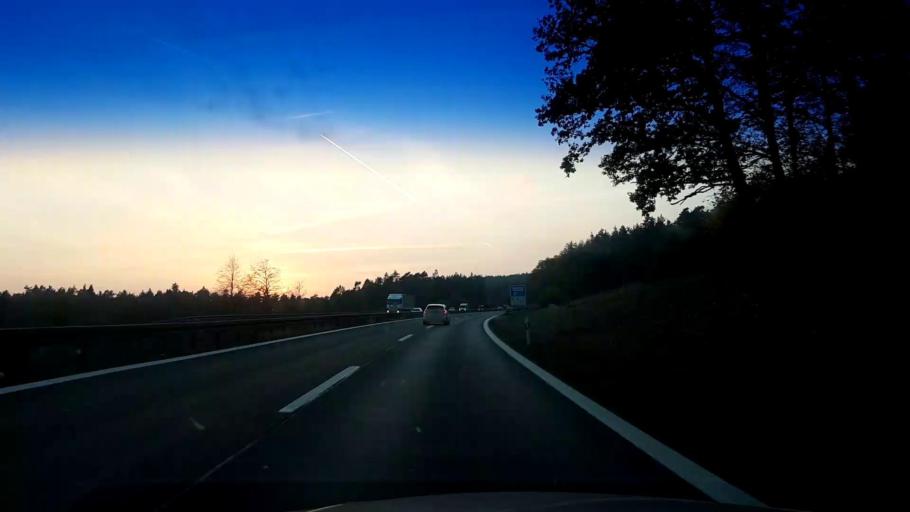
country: DE
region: Bavaria
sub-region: Upper Franconia
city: Neudrossenfeld
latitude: 50.0254
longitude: 11.4486
